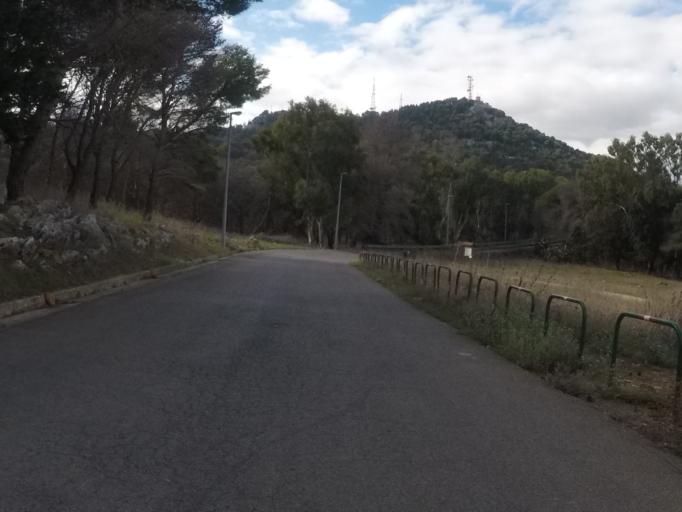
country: IT
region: Sicily
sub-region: Palermo
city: Palermo
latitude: 38.1738
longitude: 13.3572
